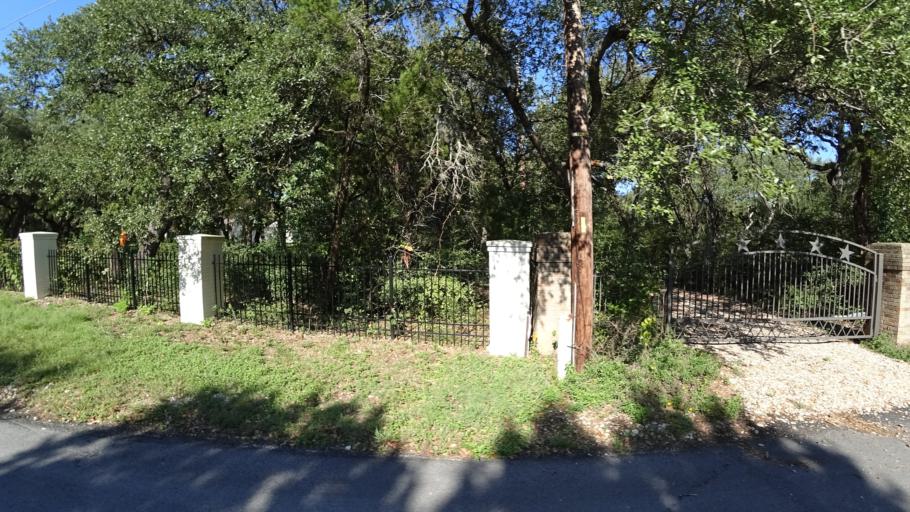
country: US
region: Texas
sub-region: Travis County
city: Rollingwood
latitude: 30.2695
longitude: -97.8151
